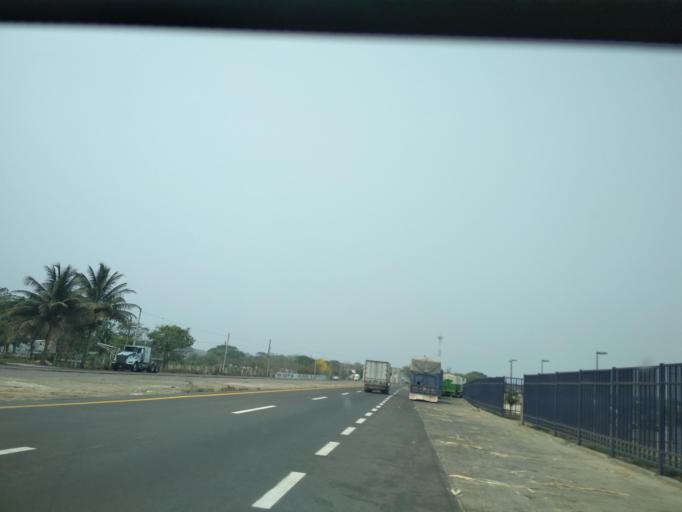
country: MX
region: Veracruz
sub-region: Veracruz
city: Delfino Victoria (Santa Fe)
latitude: 19.2001
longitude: -96.2705
